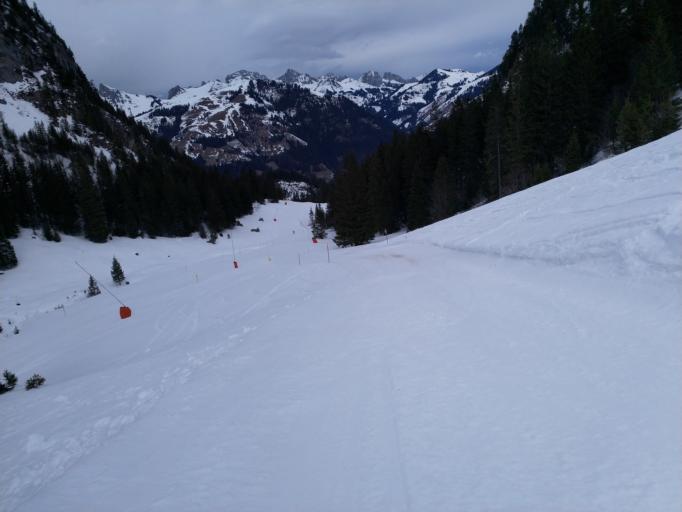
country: CH
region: Bern
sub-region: Obersimmental-Saanen District
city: Saanen
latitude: 46.4629
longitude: 7.2235
